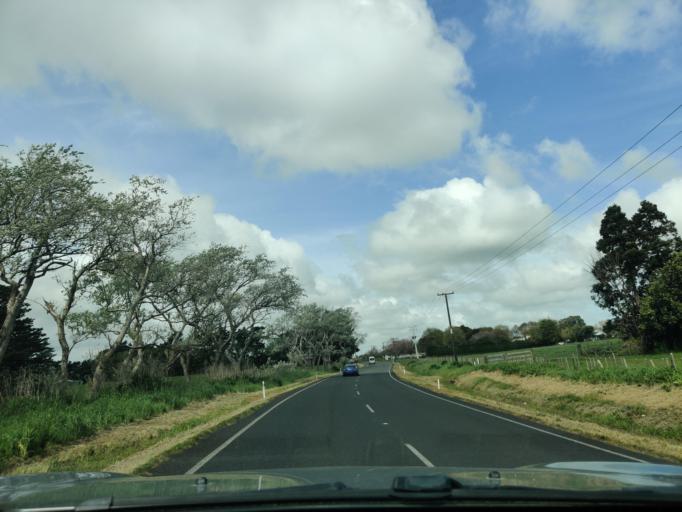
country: NZ
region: Taranaki
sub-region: South Taranaki District
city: Patea
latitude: -39.8074
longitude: 174.7592
